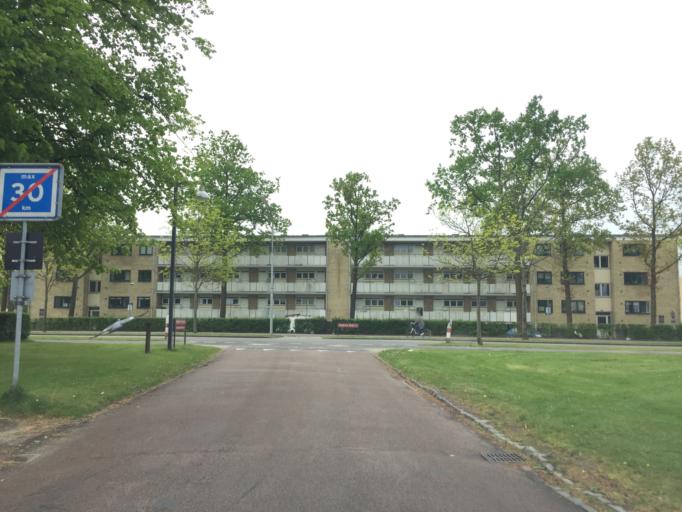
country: DK
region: Capital Region
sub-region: Rodovre Kommune
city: Rodovre
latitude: 55.6811
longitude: 12.4507
